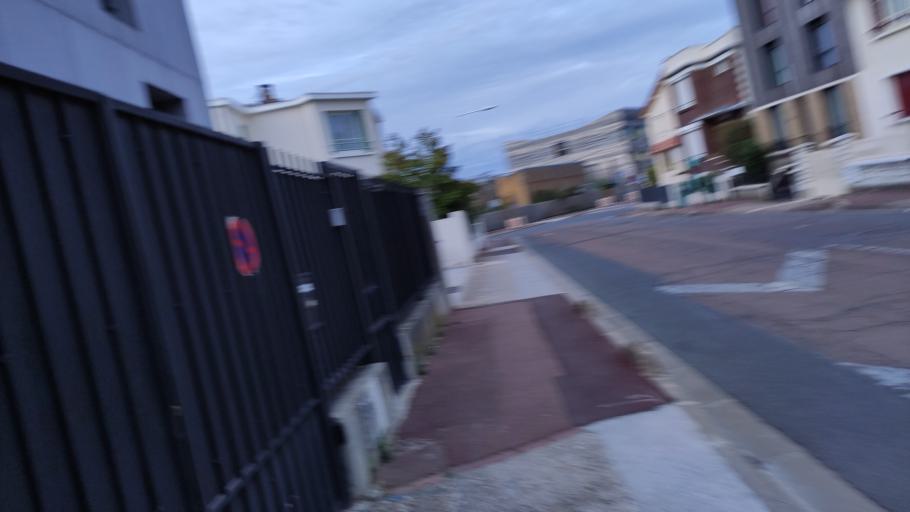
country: FR
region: Ile-de-France
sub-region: Departement des Hauts-de-Seine
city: Clamart
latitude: 48.8149
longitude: 2.2647
